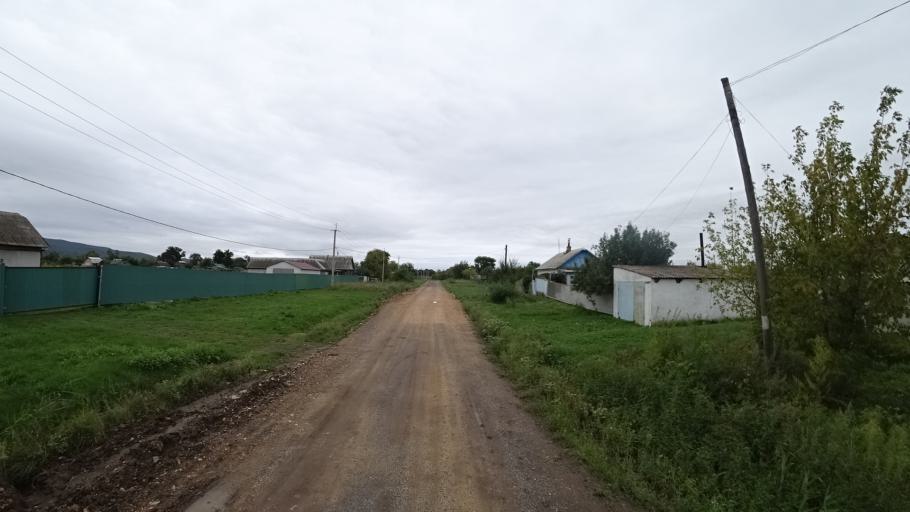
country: RU
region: Primorskiy
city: Chernigovka
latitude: 44.3386
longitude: 132.5611
